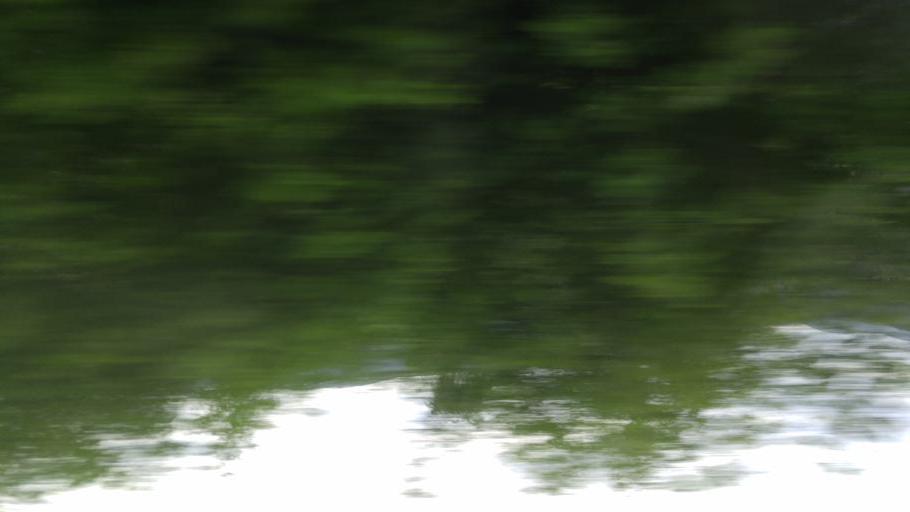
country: NO
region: Nord-Trondelag
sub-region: Meraker
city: Meraker
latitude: 63.4191
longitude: 11.7559
